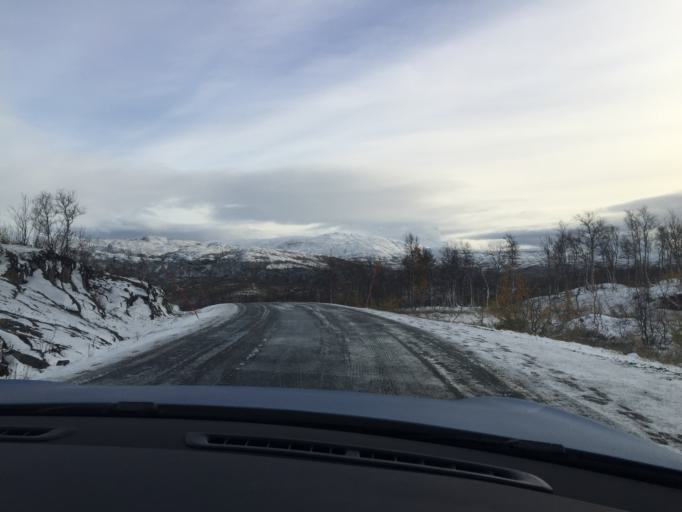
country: NO
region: Nordland
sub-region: Sorfold
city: Straumen
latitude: 67.0892
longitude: 16.0186
